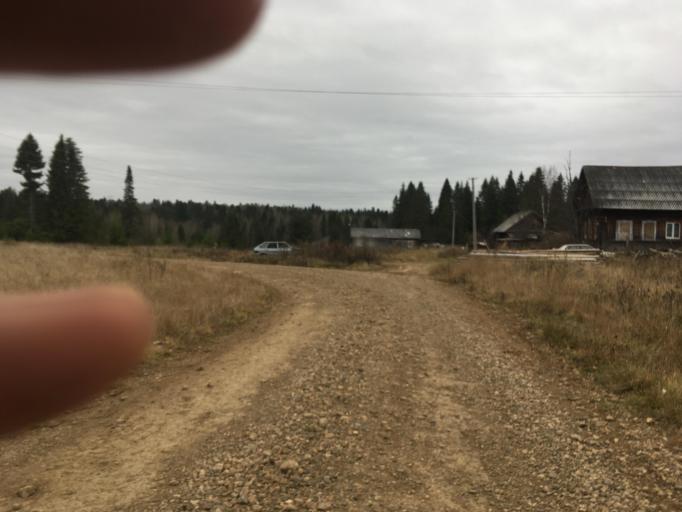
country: RU
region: Perm
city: Komarikhinskiy
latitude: 58.0886
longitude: 57.1089
